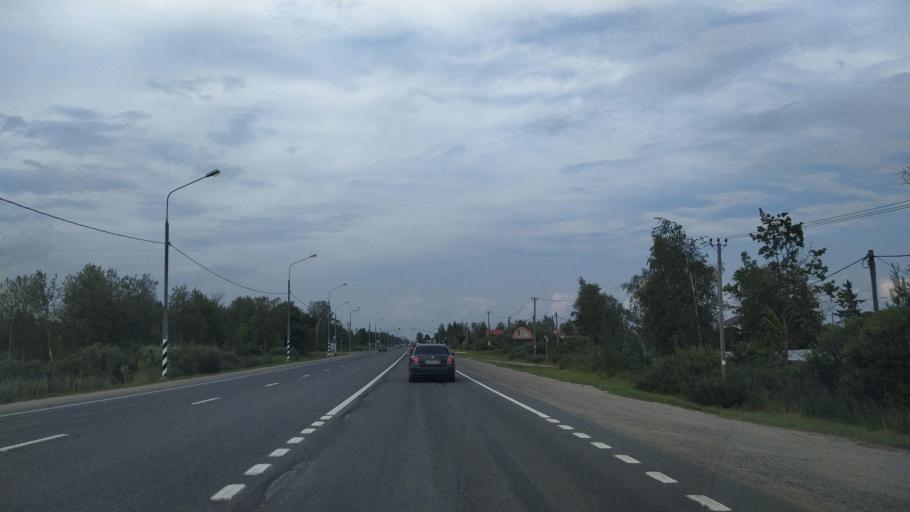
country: RU
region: Novgorod
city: Pankovka
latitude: 58.4828
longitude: 31.1888
